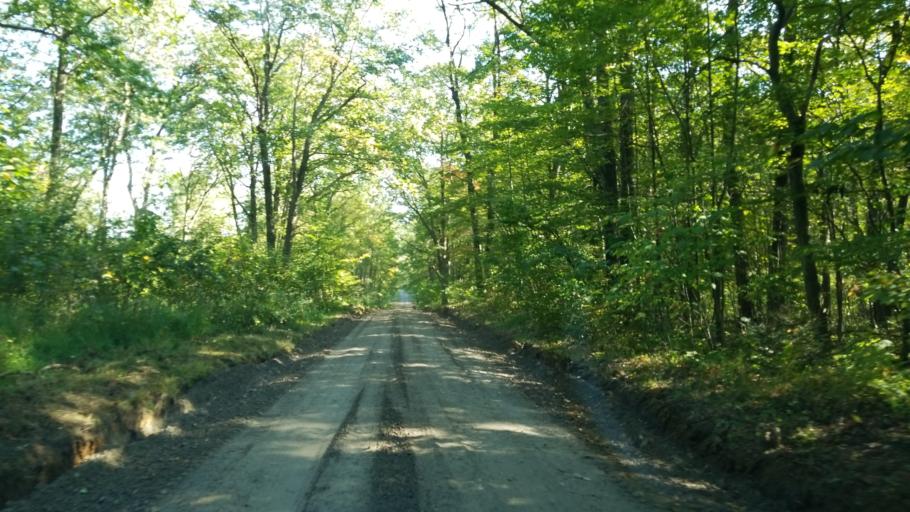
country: US
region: Pennsylvania
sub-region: Clearfield County
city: Curwensville
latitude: 41.1209
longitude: -78.5698
